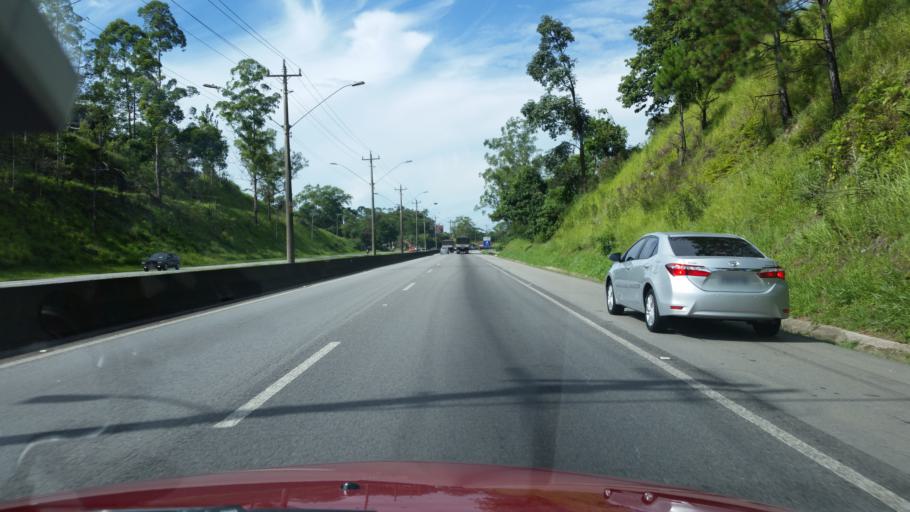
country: BR
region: Sao Paulo
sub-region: Sao Lourenco Da Serra
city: Sao Lourenco da Serra
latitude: -23.8624
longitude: -46.9476
